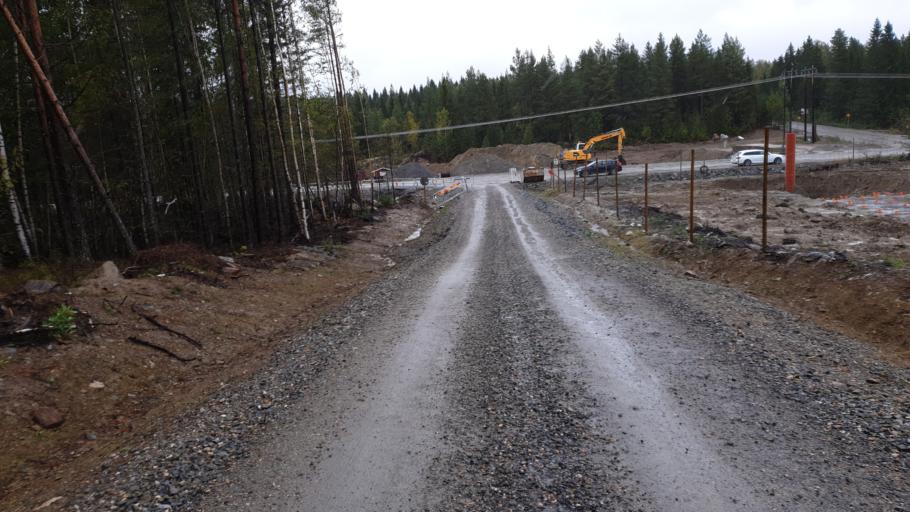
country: SE
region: Vaesterbotten
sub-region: Skelleftea Kommun
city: Soedra Bergsbyn
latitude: 64.7401
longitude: 21.0754
